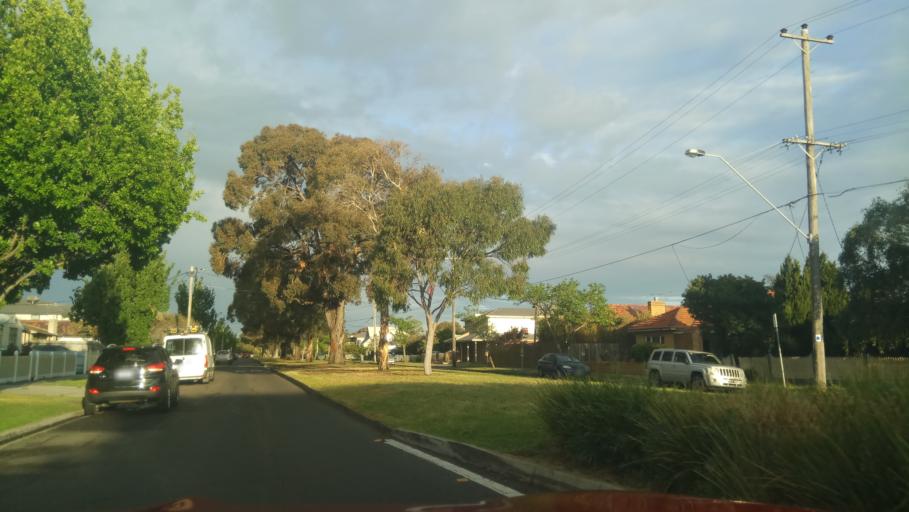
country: AU
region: Victoria
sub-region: Hobsons Bay
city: Williamstown North
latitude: -37.8471
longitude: 144.8687
